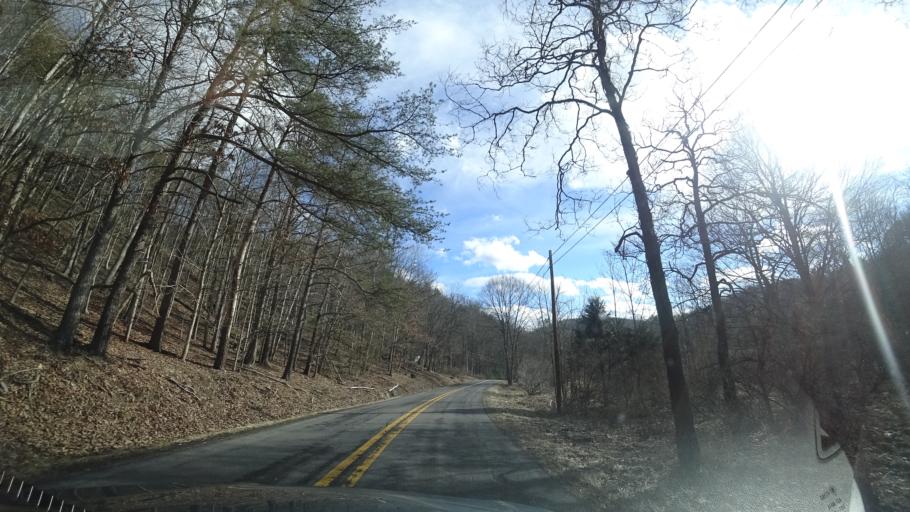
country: US
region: Virginia
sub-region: Shenandoah County
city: Basye
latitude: 38.8876
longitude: -78.8927
